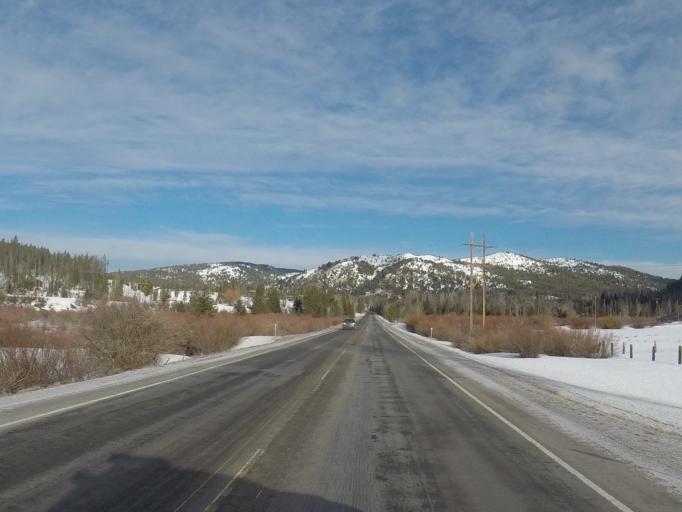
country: US
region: Montana
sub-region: Deer Lodge County
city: Anaconda
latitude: 46.1634
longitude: -113.1474
